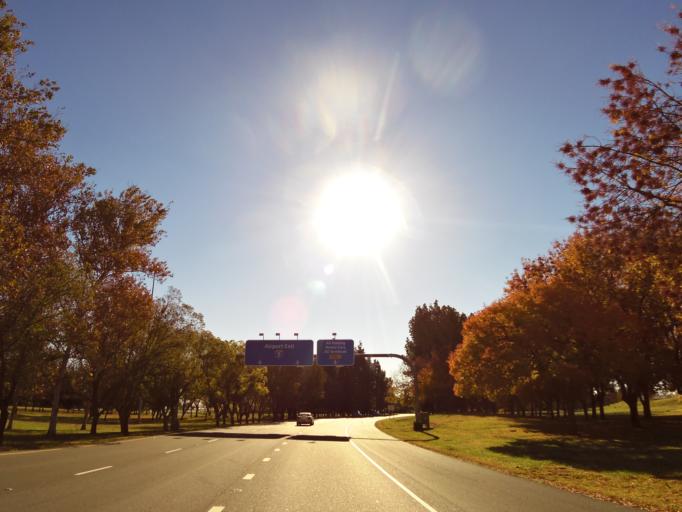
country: US
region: California
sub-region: Yolo County
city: West Sacramento
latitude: 38.6815
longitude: -121.5924
